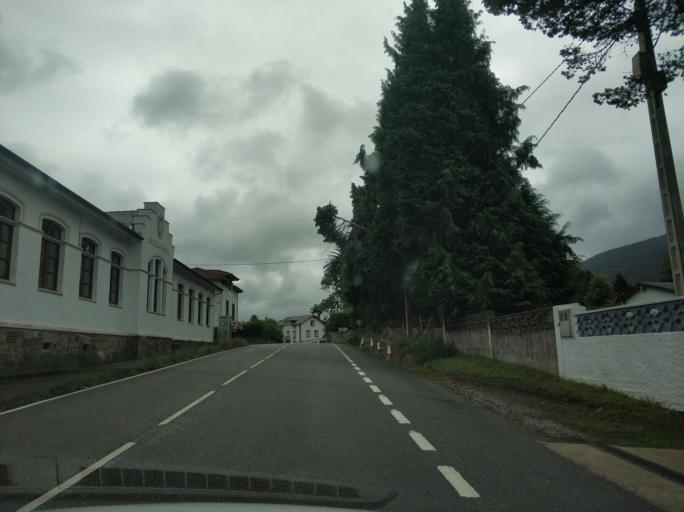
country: ES
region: Asturias
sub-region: Province of Asturias
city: Salas
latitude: 43.5446
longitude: -6.3896
